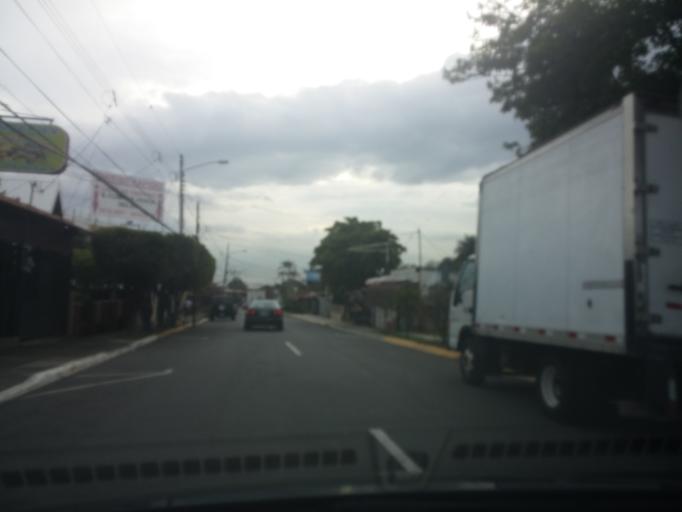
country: CR
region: Heredia
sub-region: Canton de Belen
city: San Antonio
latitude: 9.9793
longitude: -84.1900
